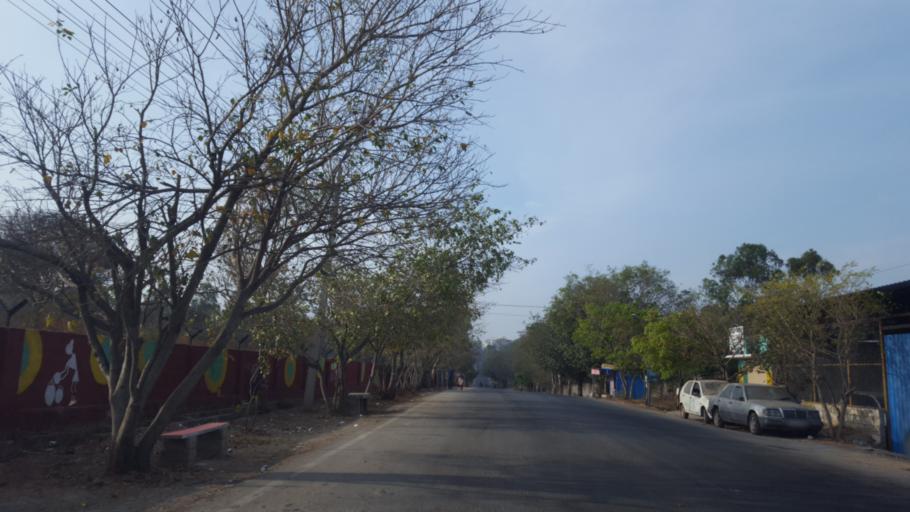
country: IN
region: Karnataka
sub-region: Bangalore Urban
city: Bangalore
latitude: 12.9120
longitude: 77.5004
